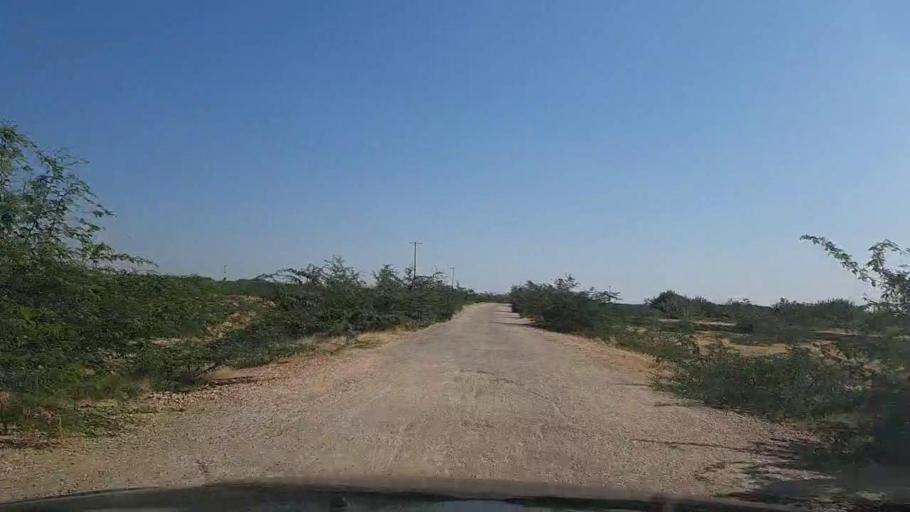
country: PK
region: Sindh
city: Thatta
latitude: 24.6294
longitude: 67.8394
